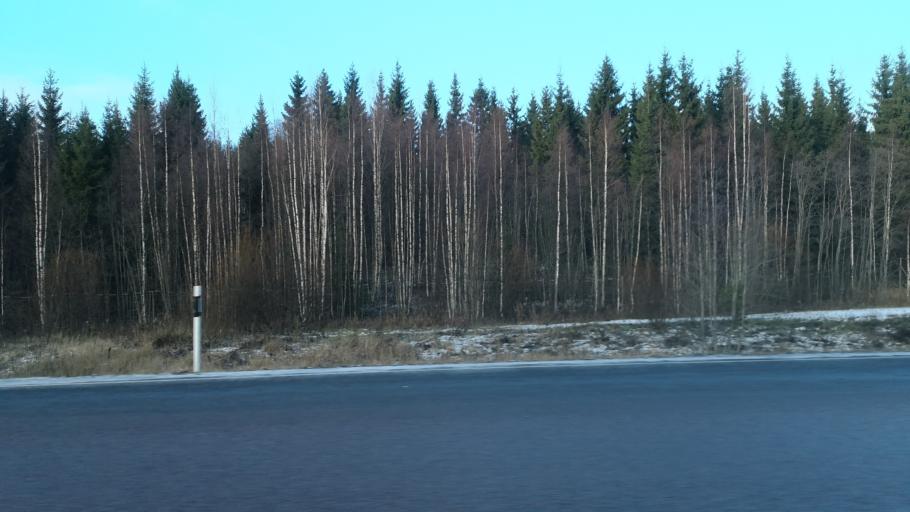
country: FI
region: Paijanne Tavastia
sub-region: Lahti
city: Heinola
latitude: 61.3503
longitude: 26.2169
